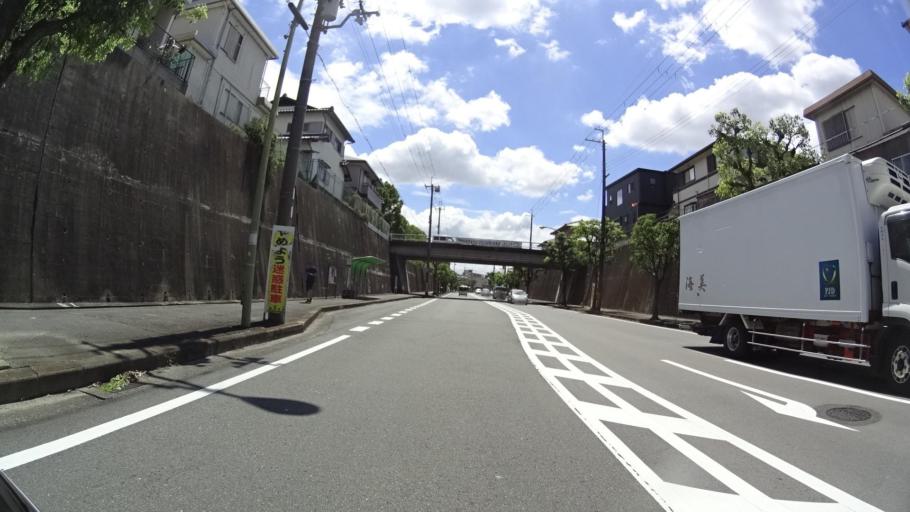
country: JP
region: Kyoto
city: Yawata
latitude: 34.8710
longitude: 135.6902
